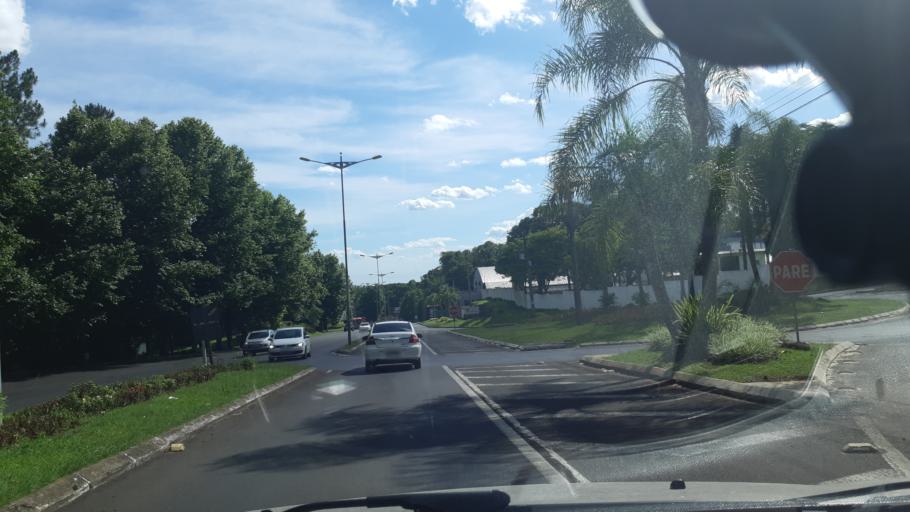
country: BR
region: Rio Grande do Sul
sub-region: Ivoti
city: Ivoti
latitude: -29.6246
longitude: -51.1353
